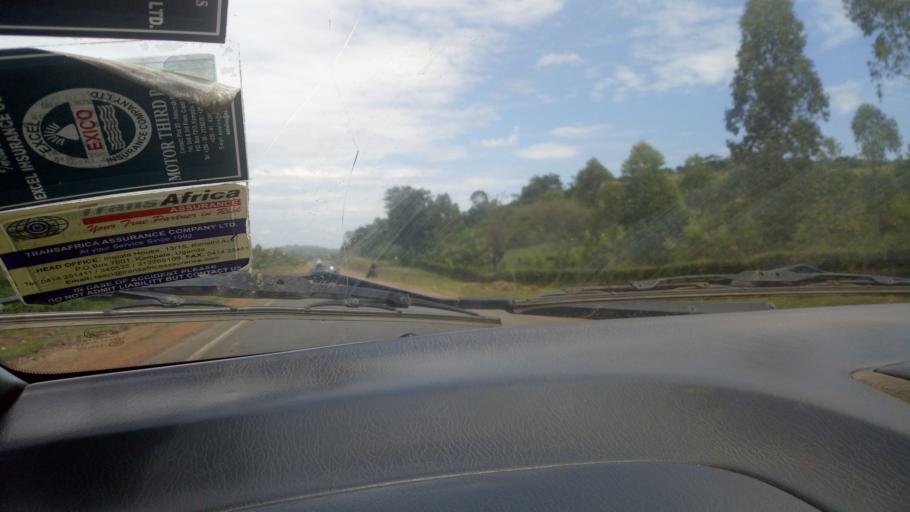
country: UG
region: Western Region
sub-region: Mbarara District
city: Bwizibwera
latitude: -0.3892
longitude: 30.5656
